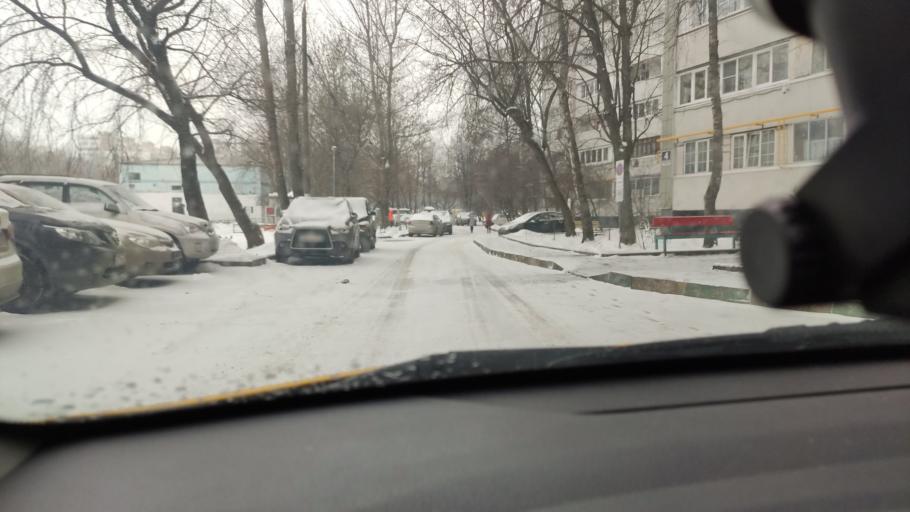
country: RU
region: Moskovskaya
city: Biryulevo Zapadnoye
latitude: 55.6009
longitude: 37.6607
